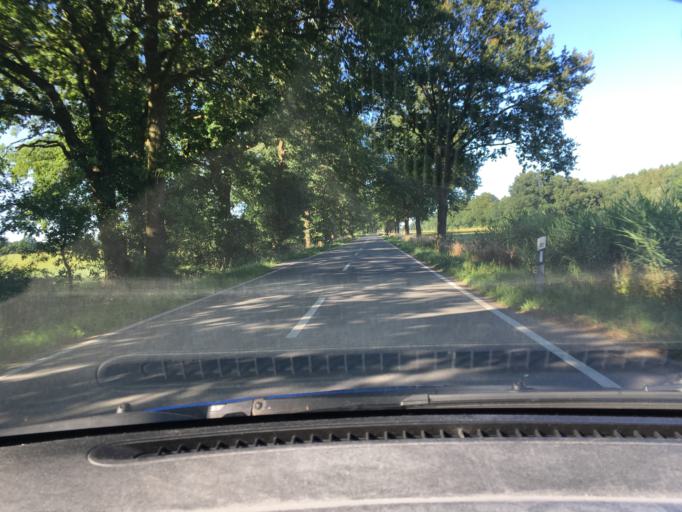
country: DE
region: Mecklenburg-Vorpommern
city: Boizenburg
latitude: 53.3343
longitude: 10.6835
